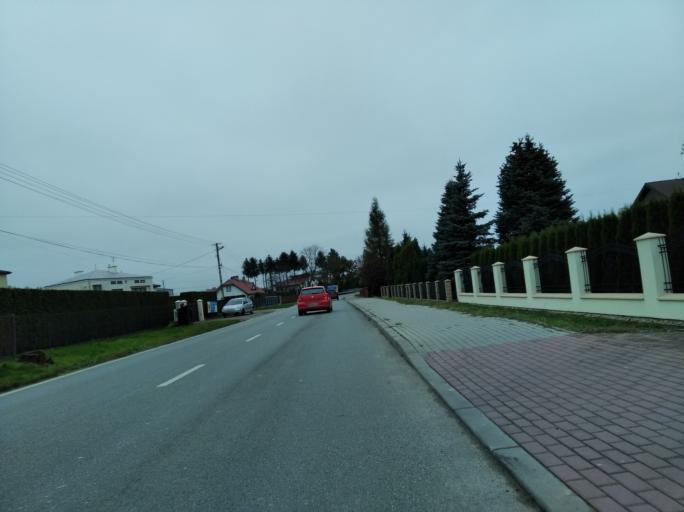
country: PL
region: Subcarpathian Voivodeship
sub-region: Powiat krosnienski
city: Chorkowka
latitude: 49.6785
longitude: 21.7128
